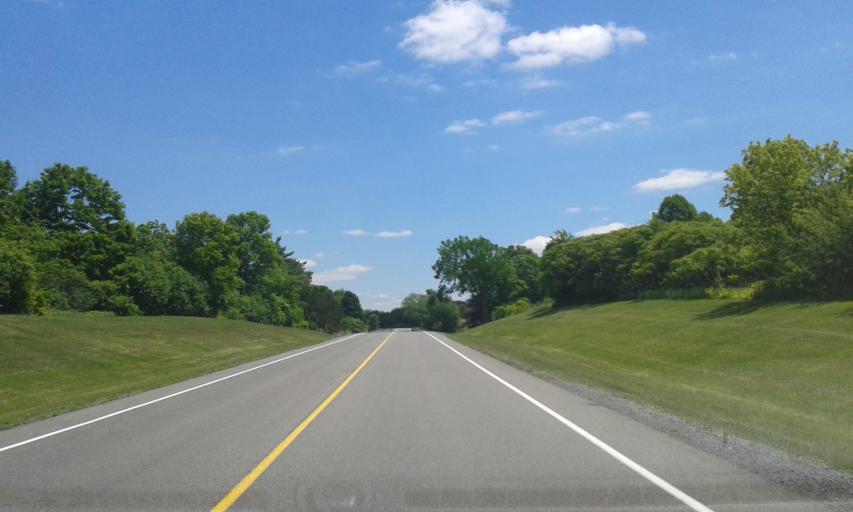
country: US
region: New York
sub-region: St. Lawrence County
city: Massena
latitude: 44.9951
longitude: -74.9383
